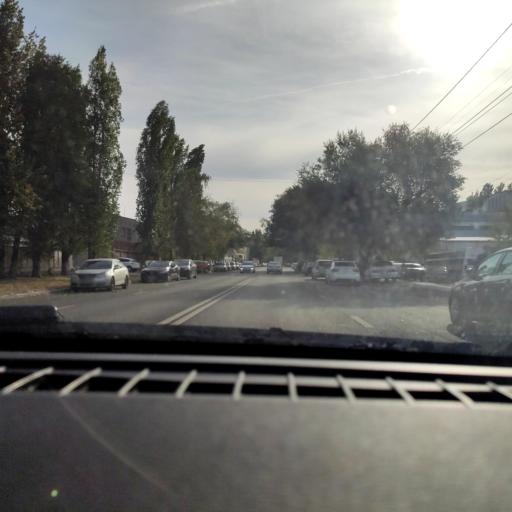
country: RU
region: Voronezj
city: Voronezh
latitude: 51.6782
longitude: 39.2526
